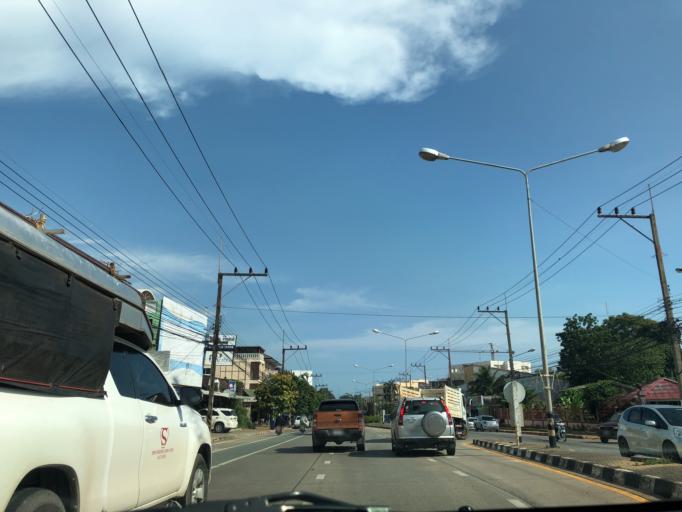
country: TH
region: Krabi
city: Krabi
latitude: 8.0794
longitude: 98.9151
